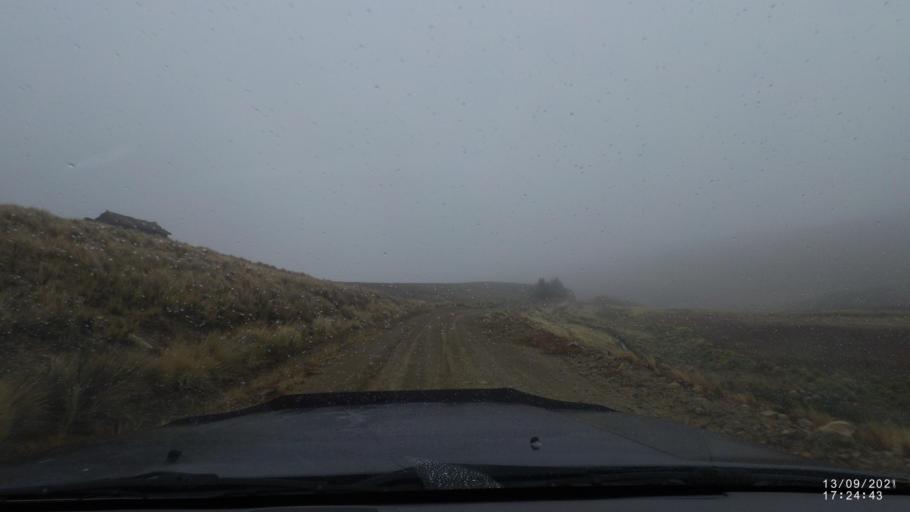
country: BO
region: Cochabamba
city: Colomi
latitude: -17.3567
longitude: -65.7779
